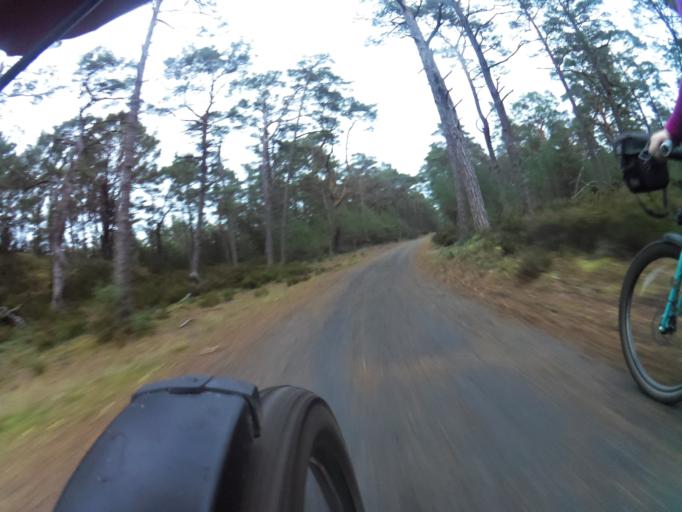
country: PL
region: Pomeranian Voivodeship
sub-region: Powiat wejherowski
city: Choczewo
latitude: 54.7935
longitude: 17.7601
